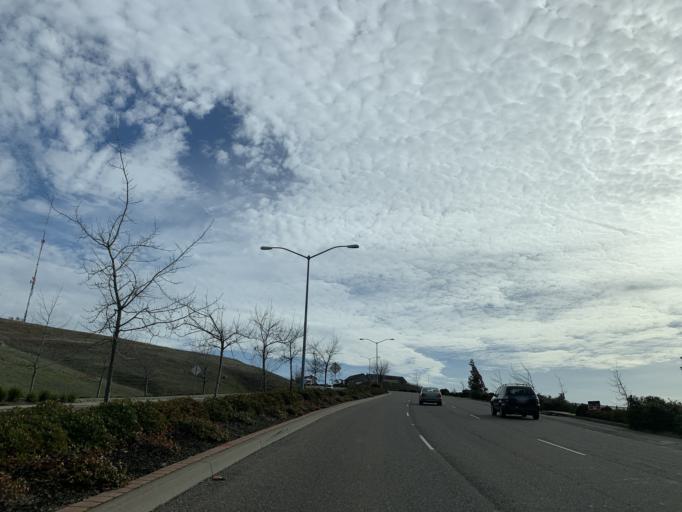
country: US
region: California
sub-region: El Dorado County
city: El Dorado Hills
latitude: 38.6476
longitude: -121.1026
